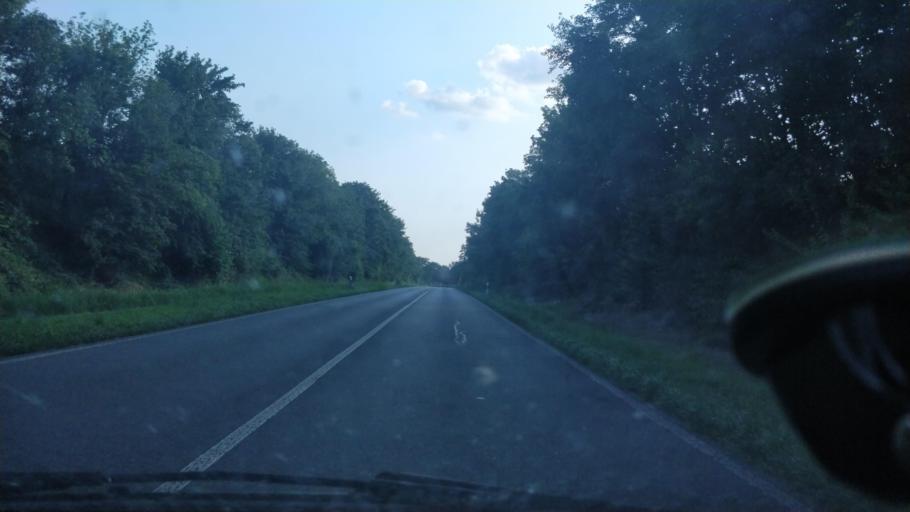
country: DE
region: North Rhine-Westphalia
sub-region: Regierungsbezirk Dusseldorf
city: Rheurdt
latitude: 51.4706
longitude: 6.4574
